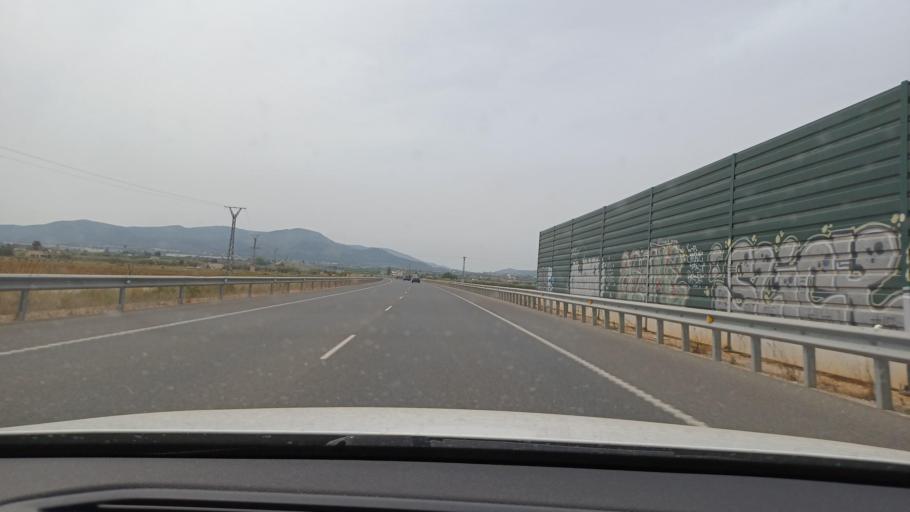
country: ES
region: Valencia
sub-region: Provincia de Castello
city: Benicarlo
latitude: 40.4224
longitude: 0.3911
